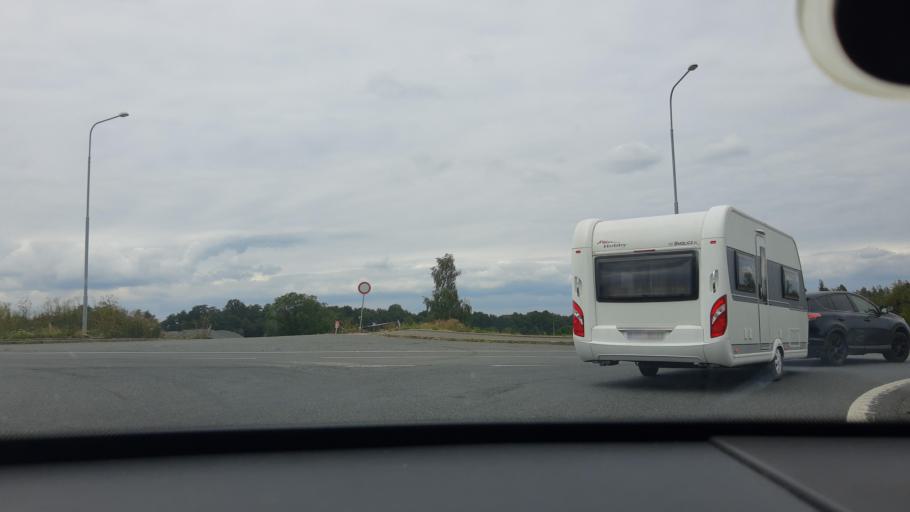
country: CZ
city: Ropice
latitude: 49.6767
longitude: 18.6040
